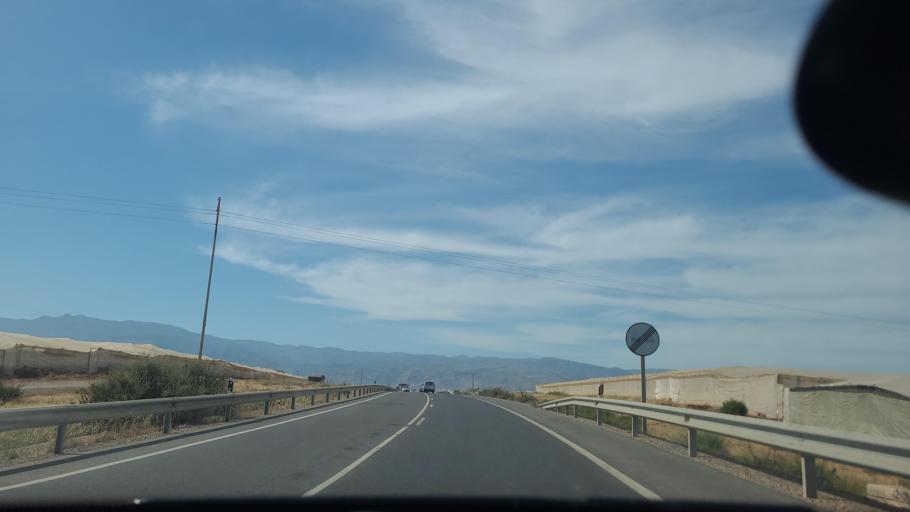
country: ES
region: Andalusia
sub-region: Provincia de Almeria
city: Roquetas de Mar
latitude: 36.7385
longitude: -2.6243
